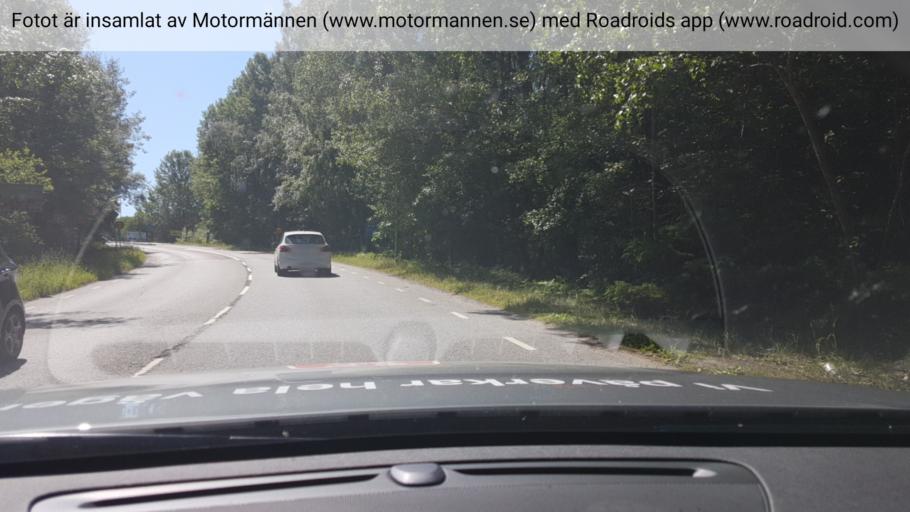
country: SE
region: Stockholm
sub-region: Haninge Kommun
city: Handen
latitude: 59.1960
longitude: 18.1394
